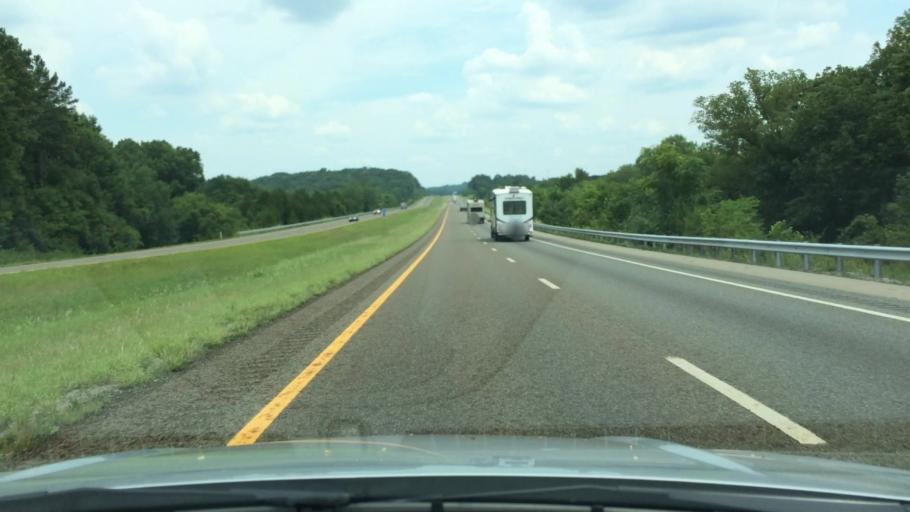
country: US
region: Tennessee
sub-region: Maury County
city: Columbia
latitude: 35.5998
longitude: -86.9016
